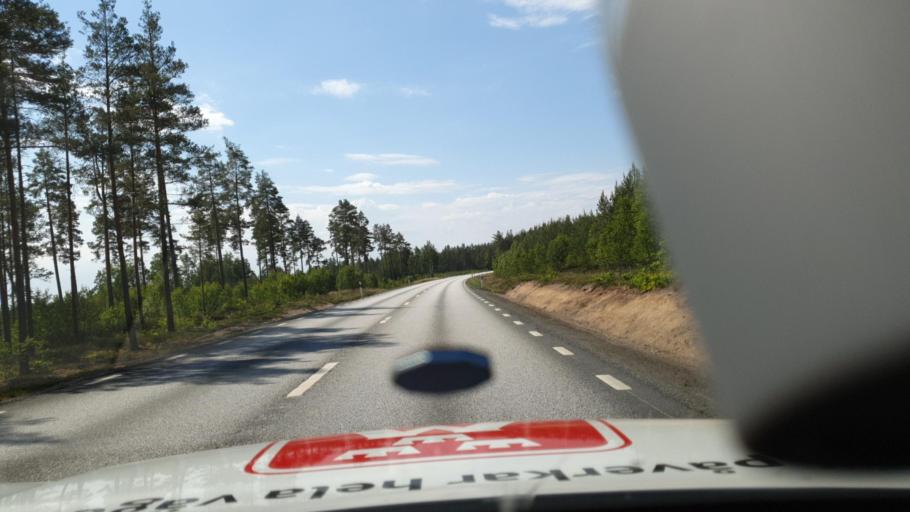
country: SE
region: Joenkoeping
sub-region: Habo Kommun
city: Habo
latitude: 58.0385
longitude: 14.1789
